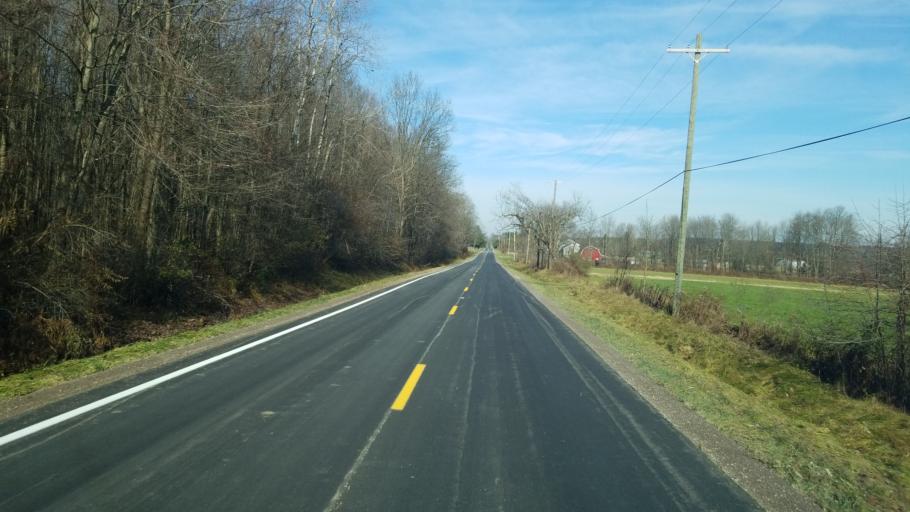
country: US
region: Ohio
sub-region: Ashtabula County
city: Roaming Shores
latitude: 41.7059
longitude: -80.9038
